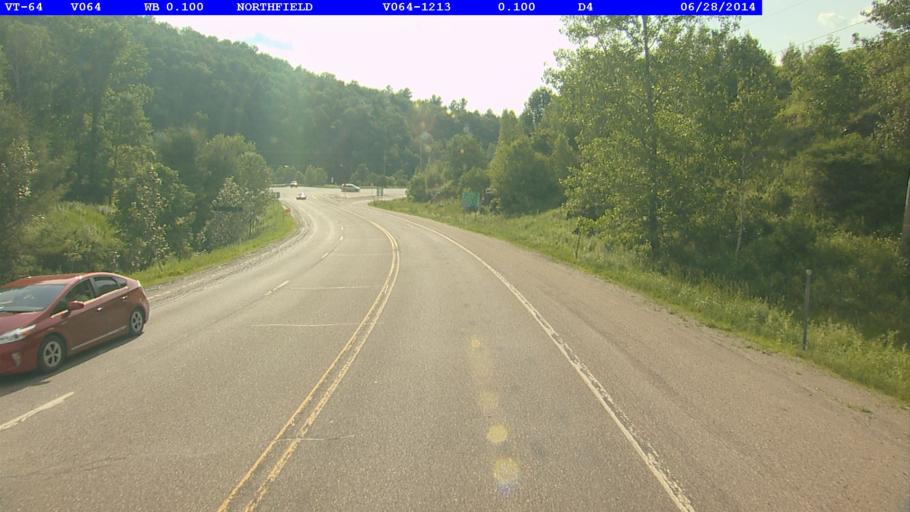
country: US
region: Vermont
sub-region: Washington County
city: Northfield
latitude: 44.1186
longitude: -72.6542
